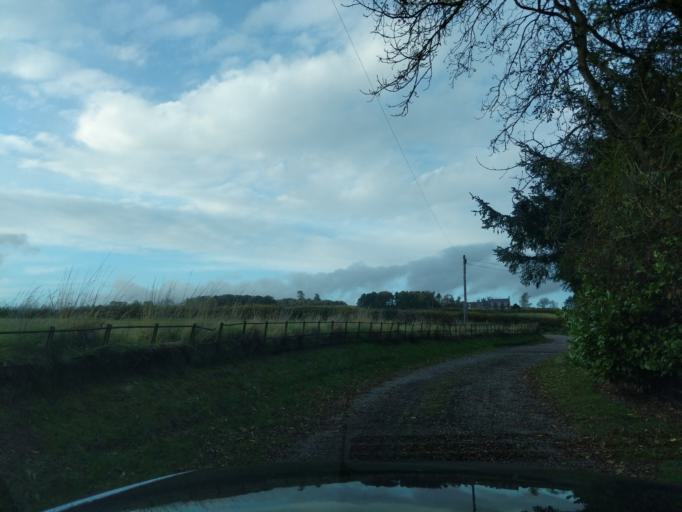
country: GB
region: Scotland
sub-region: Fife
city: Newport-On-Tay
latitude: 56.4217
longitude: -2.9137
